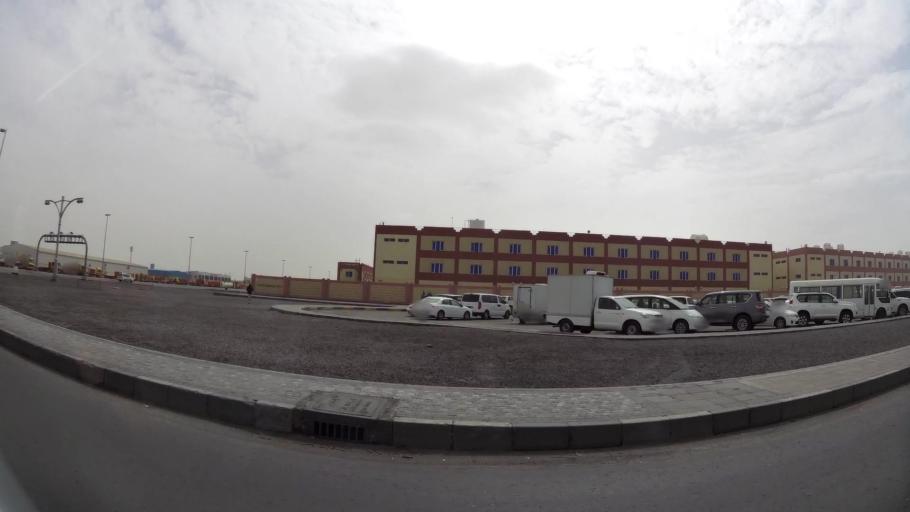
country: AE
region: Abu Dhabi
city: Abu Dhabi
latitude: 24.3452
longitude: 54.4922
